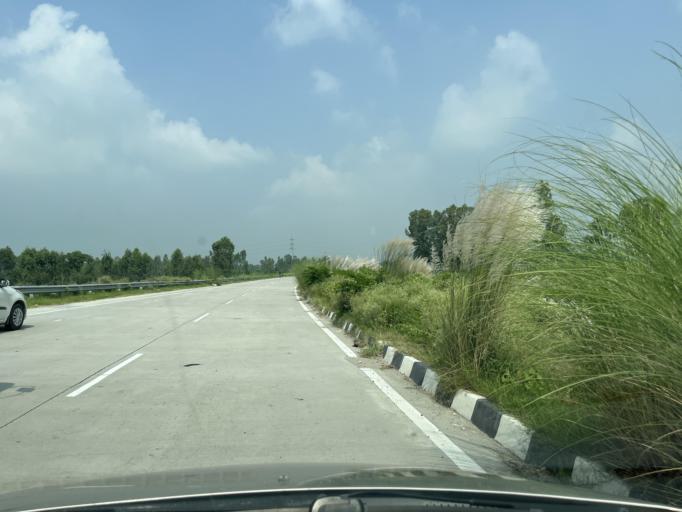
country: IN
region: Uttarakhand
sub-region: Udham Singh Nagar
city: Kashipur
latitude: 29.1639
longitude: 78.9617
